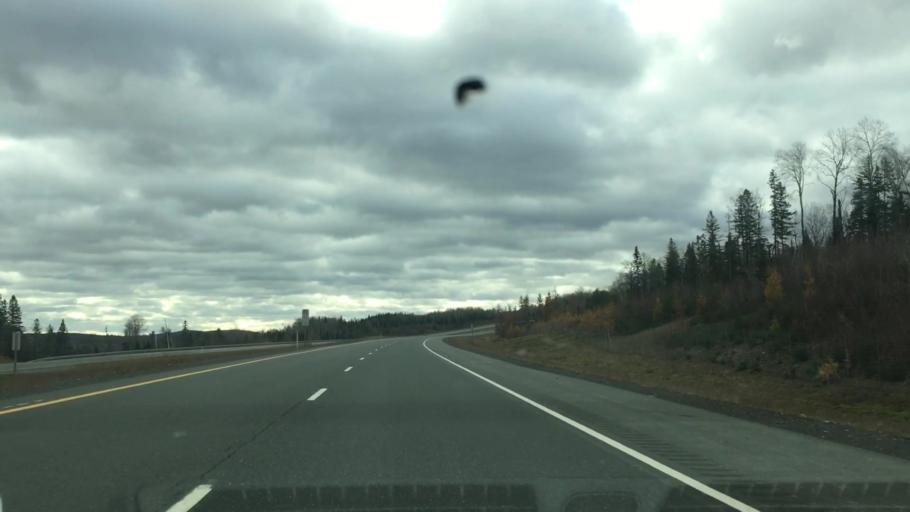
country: US
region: Maine
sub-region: Aroostook County
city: Fort Fairfield
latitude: 46.6725
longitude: -67.7294
